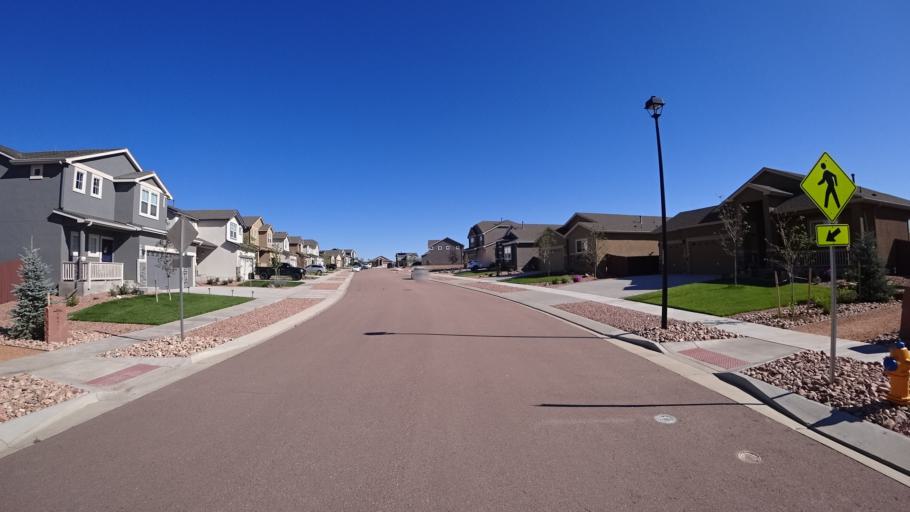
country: US
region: Colorado
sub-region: El Paso County
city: Black Forest
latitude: 38.9497
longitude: -104.6738
